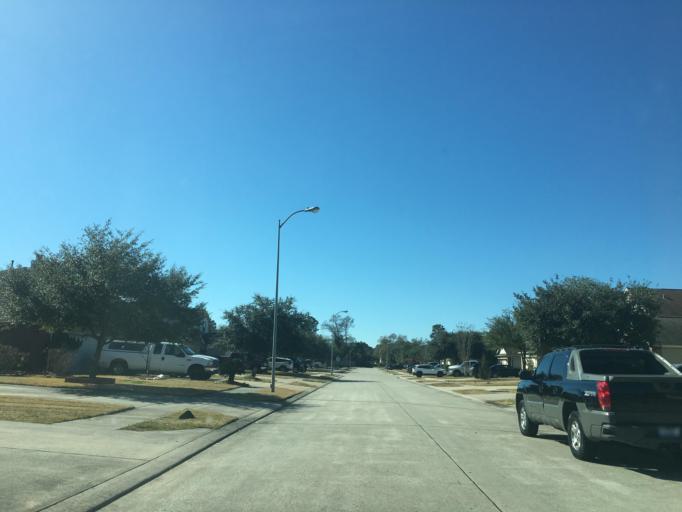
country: US
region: Texas
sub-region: Harris County
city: Spring
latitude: 30.0860
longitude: -95.4627
